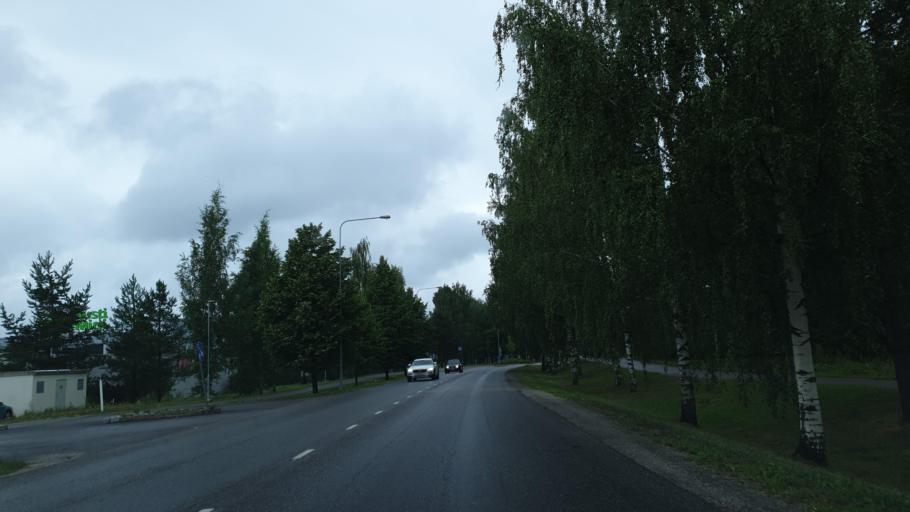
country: FI
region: Paijanne Tavastia
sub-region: Lahti
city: Lahti
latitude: 60.9627
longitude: 25.6588
